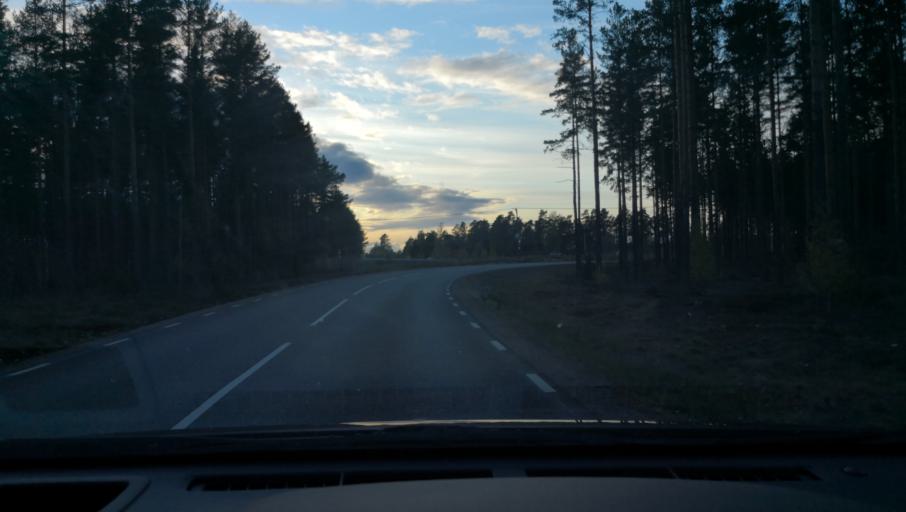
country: SE
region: OErebro
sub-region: Askersunds Kommun
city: Asbro
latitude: 58.9159
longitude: 15.0672
